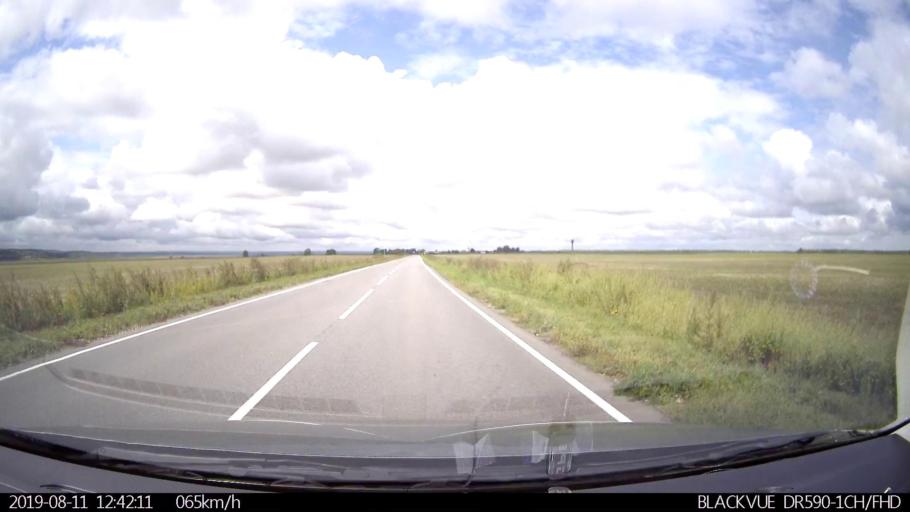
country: RU
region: Ulyanovsk
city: Ignatovka
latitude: 53.8440
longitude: 47.7545
